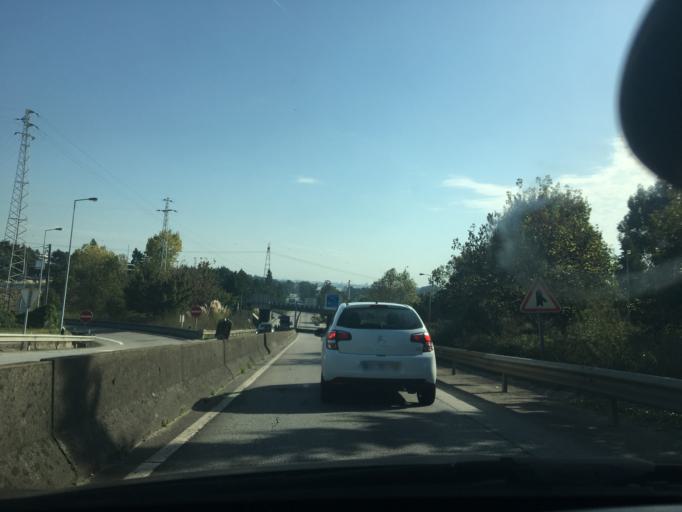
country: PT
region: Porto
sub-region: Maia
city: Gemunde
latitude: 41.2423
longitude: -8.6474
